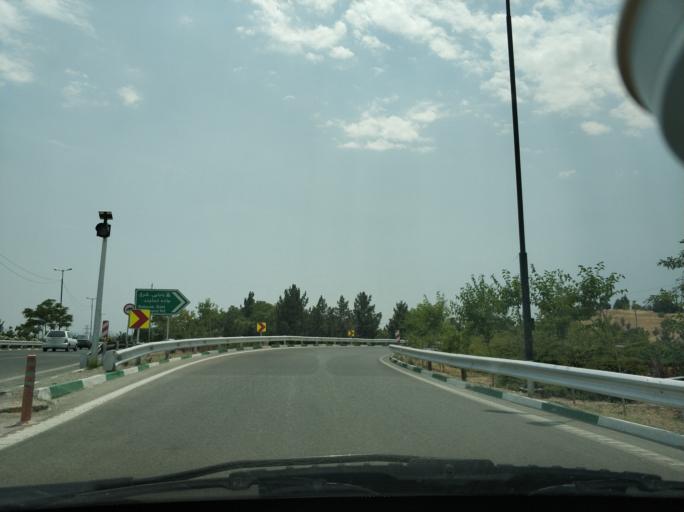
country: IR
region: Tehran
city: Tajrish
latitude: 35.7692
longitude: 51.5566
